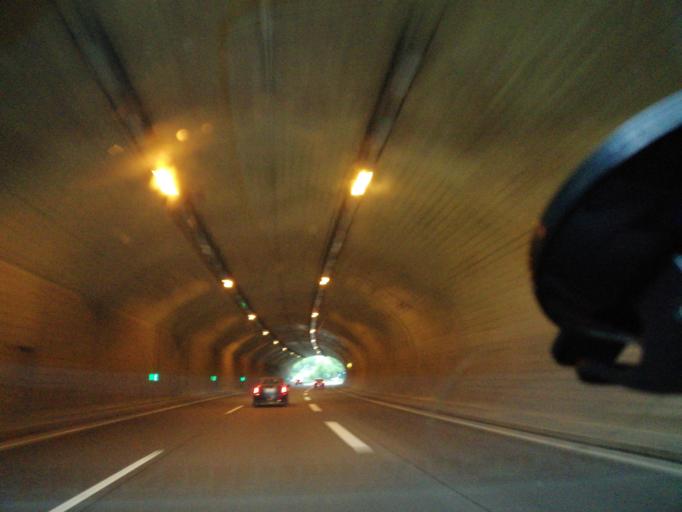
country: DE
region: North Rhine-Westphalia
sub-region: Regierungsbezirk Dusseldorf
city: Wuppertal
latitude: 51.2287
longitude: 7.1513
